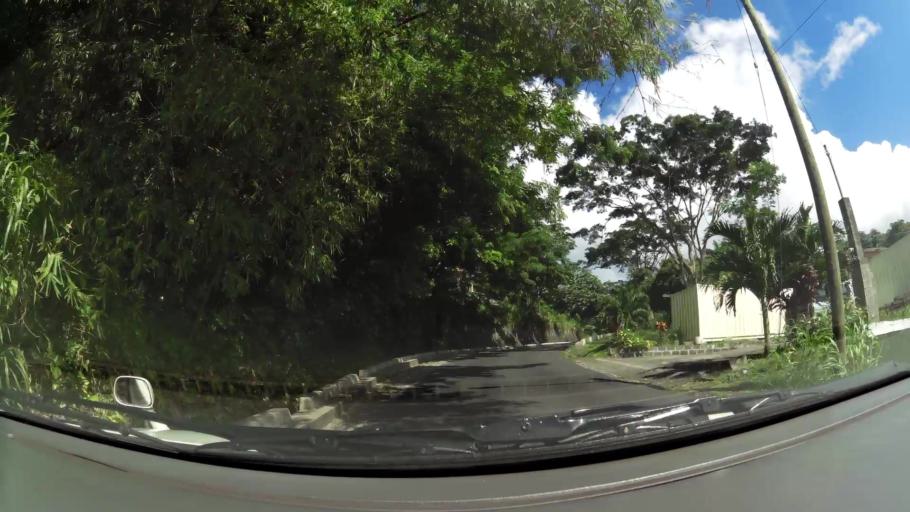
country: VC
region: Saint George
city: Kingstown
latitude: 13.1672
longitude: -61.2285
